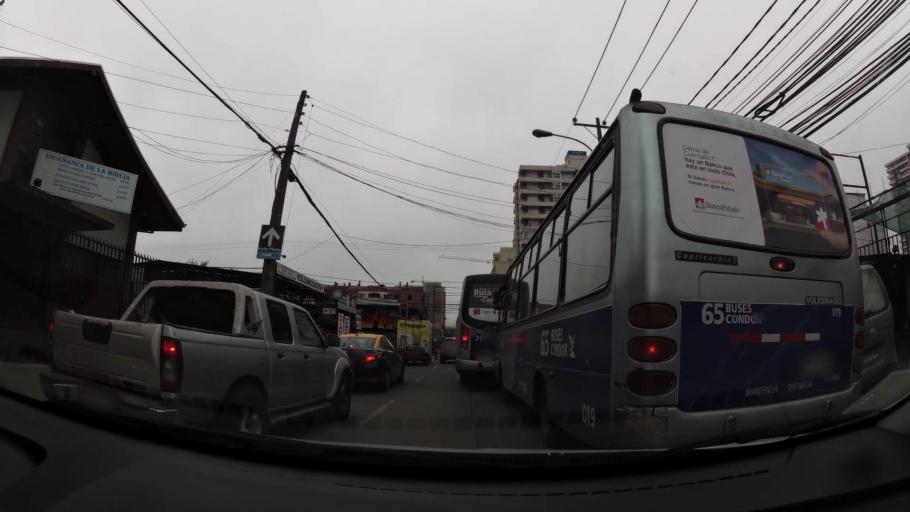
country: CL
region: Biobio
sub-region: Provincia de Concepcion
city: Concepcion
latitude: -36.8208
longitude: -73.0428
